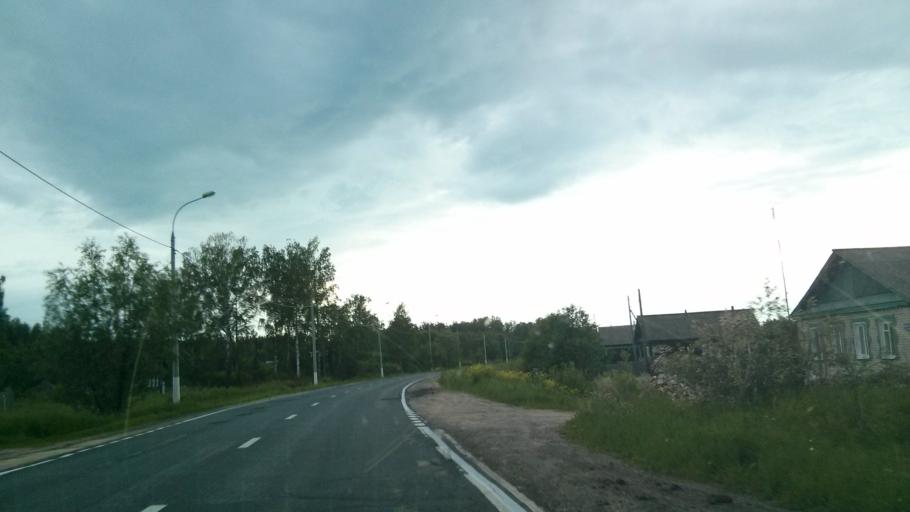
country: RU
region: Nizjnij Novgorod
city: Vacha
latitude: 55.7480
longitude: 42.5005
